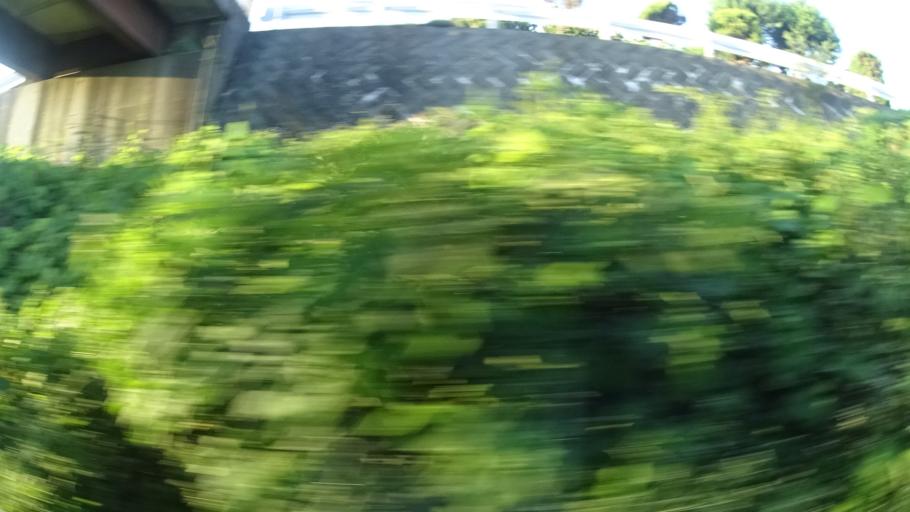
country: JP
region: Fukushima
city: Funehikimachi-funehiki
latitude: 37.4511
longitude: 140.5366
